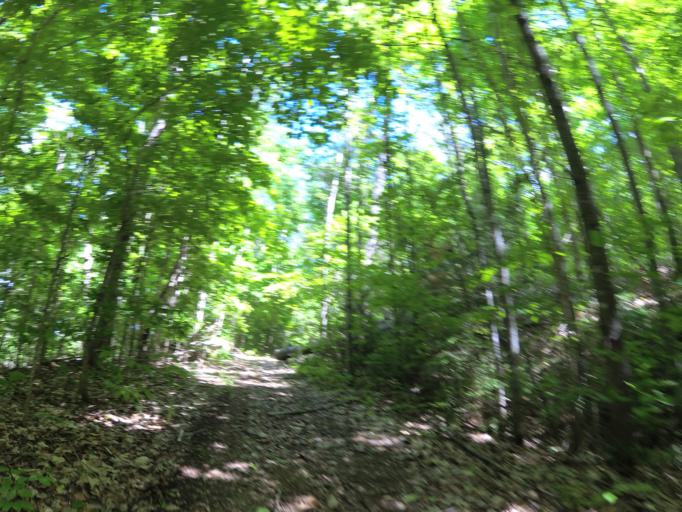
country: CA
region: Ontario
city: Renfrew
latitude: 45.0638
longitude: -76.8402
